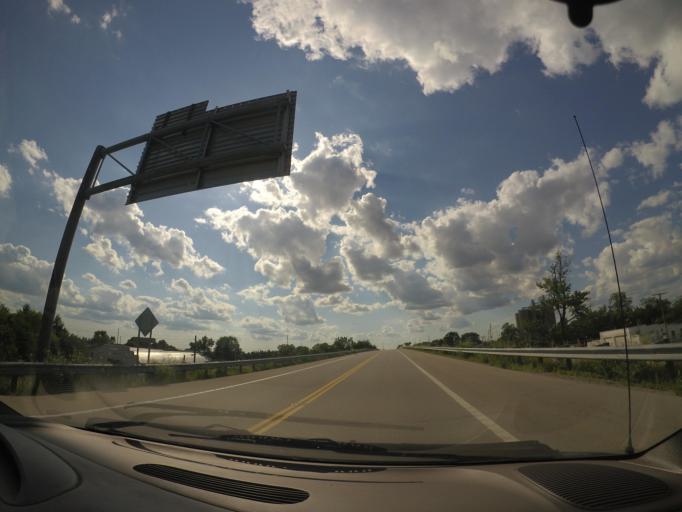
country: US
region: Ohio
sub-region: Wood County
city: Luckey
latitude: 41.4948
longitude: -83.4713
